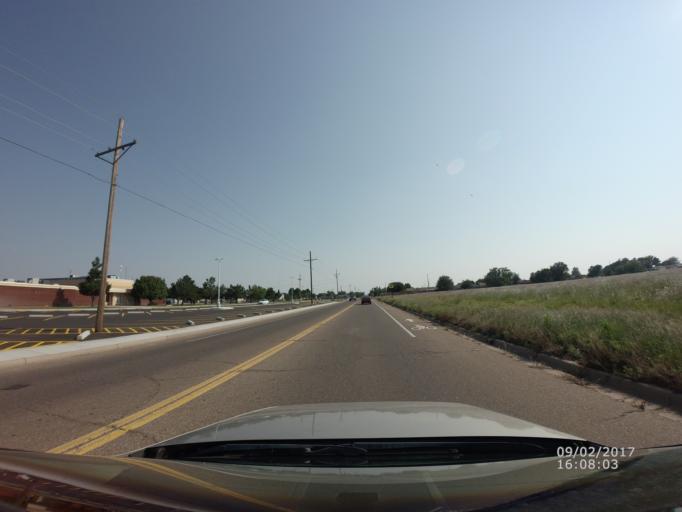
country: US
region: New Mexico
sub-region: Curry County
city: Clovis
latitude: 34.4330
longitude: -103.2141
